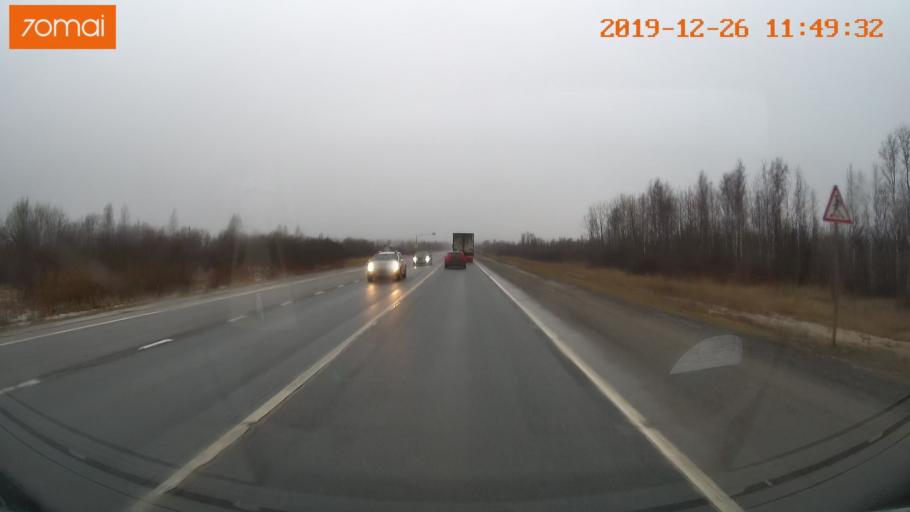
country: RU
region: Vologda
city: Sheksna
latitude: 59.2490
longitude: 38.4183
